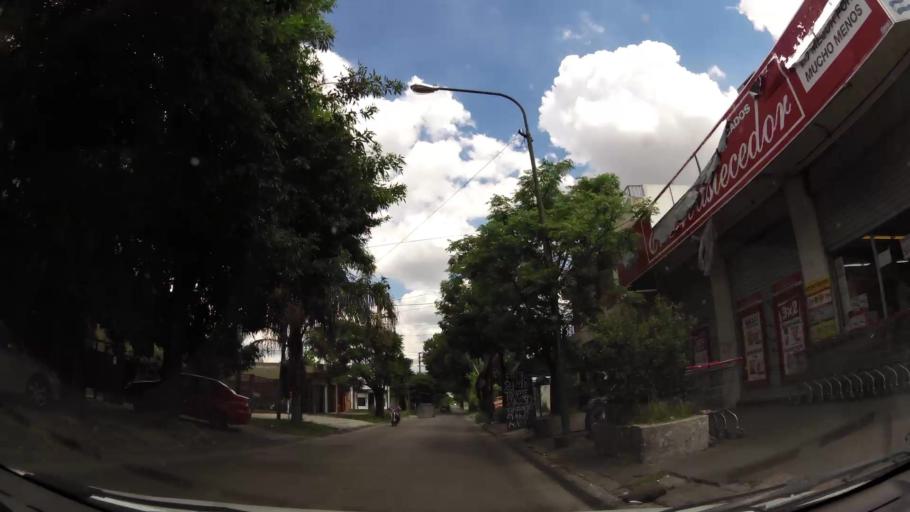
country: AR
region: Buenos Aires
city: Ituzaingo
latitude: -34.6535
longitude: -58.6752
